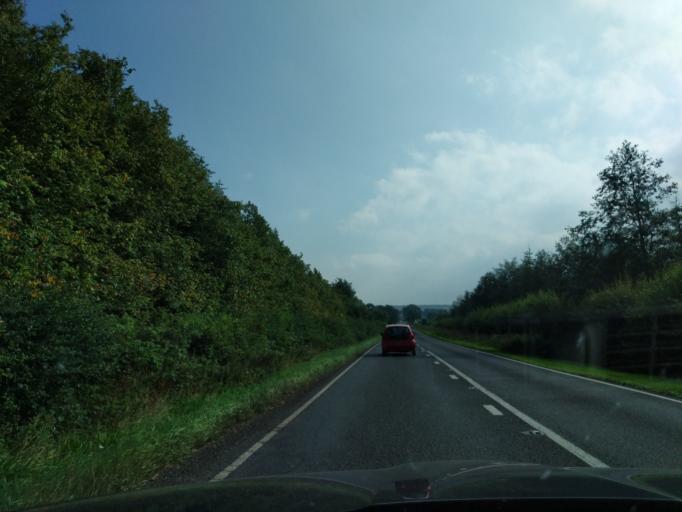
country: GB
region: England
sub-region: Northumberland
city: Longhorsley
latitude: 55.2573
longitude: -1.7730
